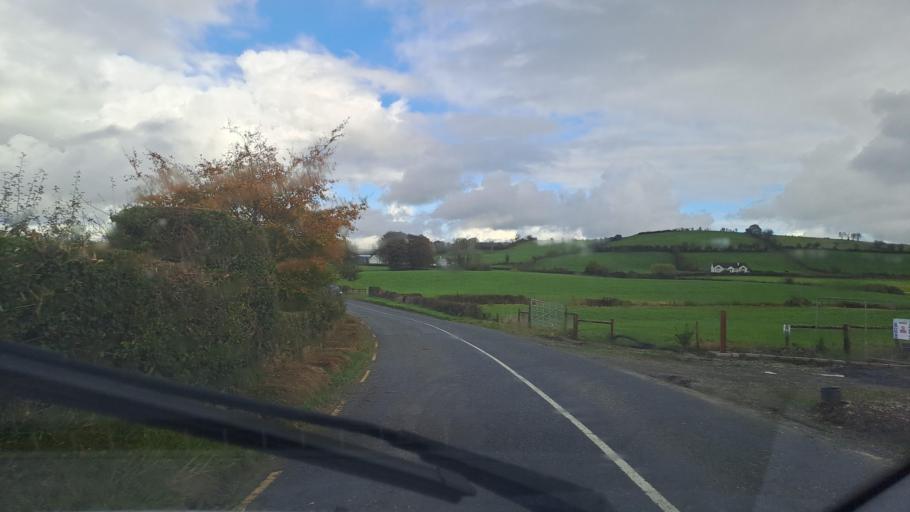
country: IE
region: Ulster
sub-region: An Cabhan
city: Mullagh
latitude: 53.8334
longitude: -6.9520
